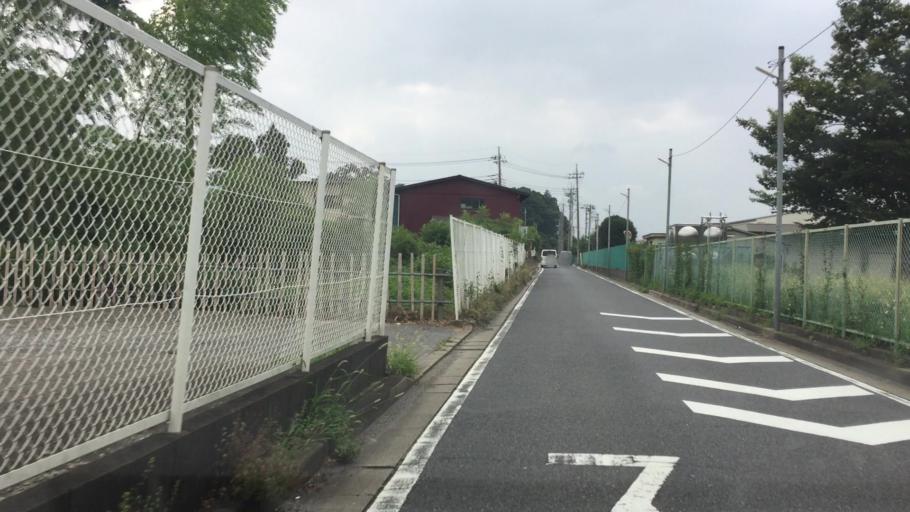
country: JP
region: Chiba
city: Kashiwa
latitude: 35.8094
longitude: 139.9579
